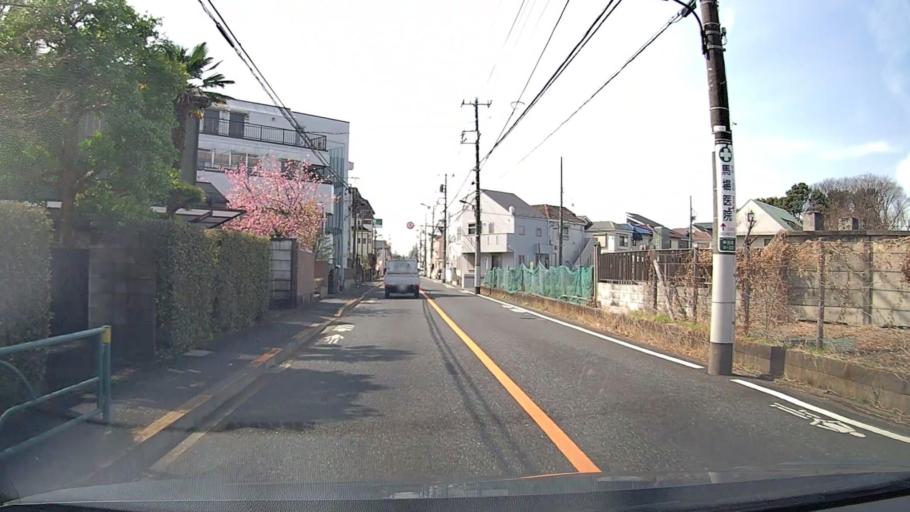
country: JP
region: Tokyo
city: Nishi-Tokyo-shi
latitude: 35.7363
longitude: 139.5525
